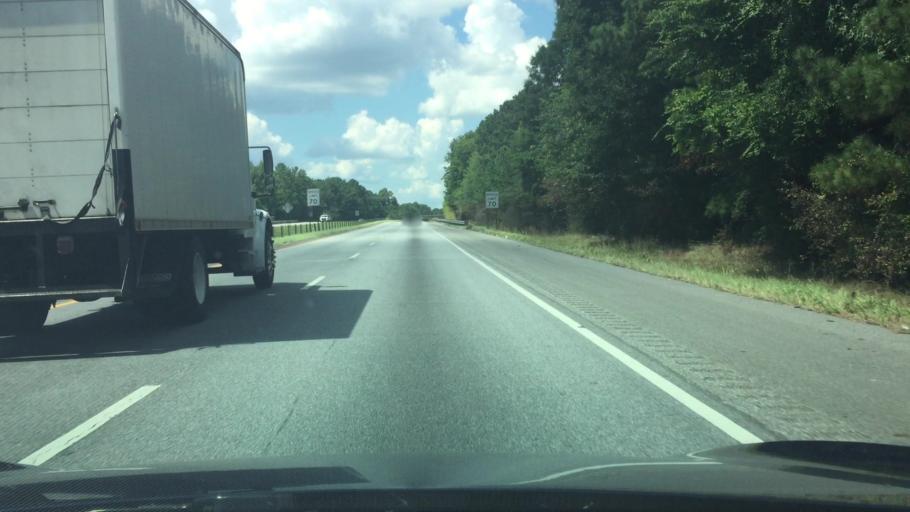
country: US
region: Alabama
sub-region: Lee County
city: Auburn
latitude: 32.5835
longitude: -85.4655
